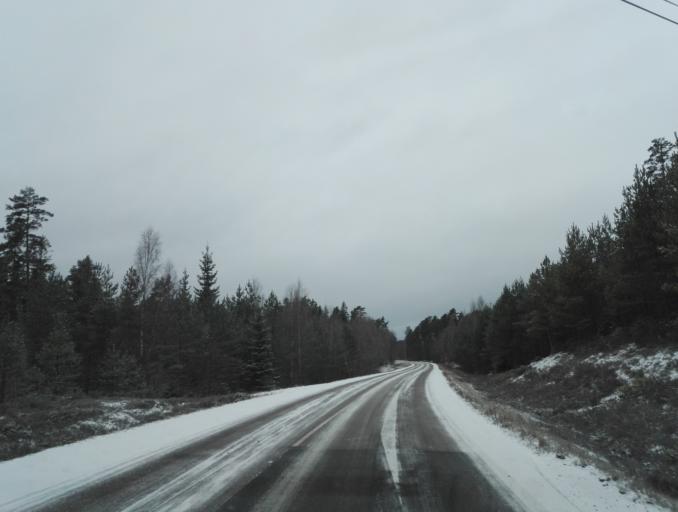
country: SE
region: Kronoberg
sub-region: Lessebo Kommun
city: Lessebo
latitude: 56.7392
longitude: 15.2590
